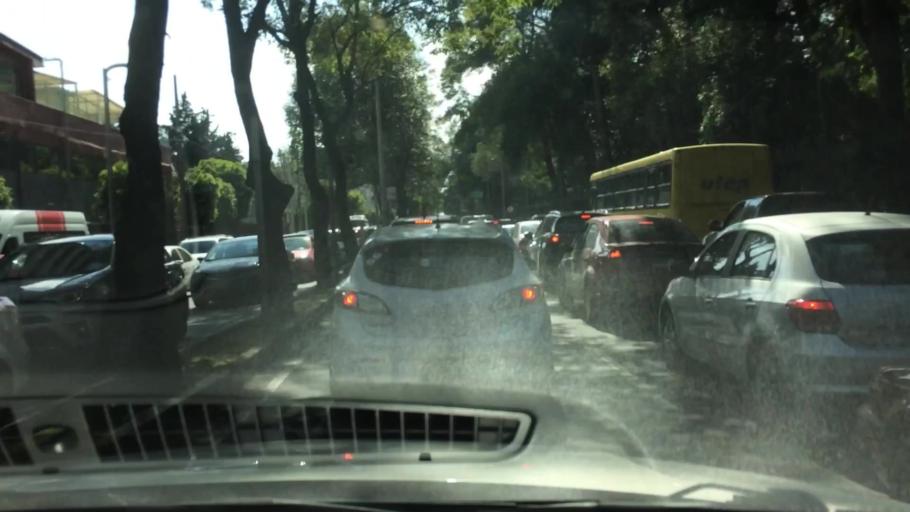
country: MX
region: Mexico City
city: Polanco
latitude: 19.4150
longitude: -99.1858
